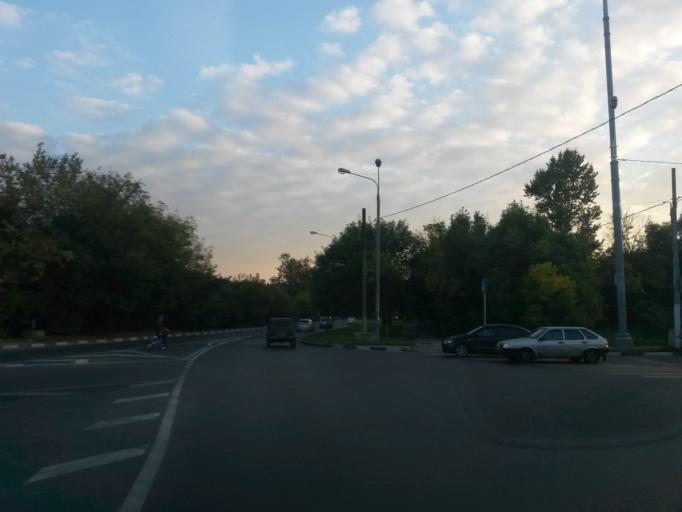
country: RU
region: Moscow
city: Orekhovo-Borisovo Severnoye
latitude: 55.6325
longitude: 37.6847
